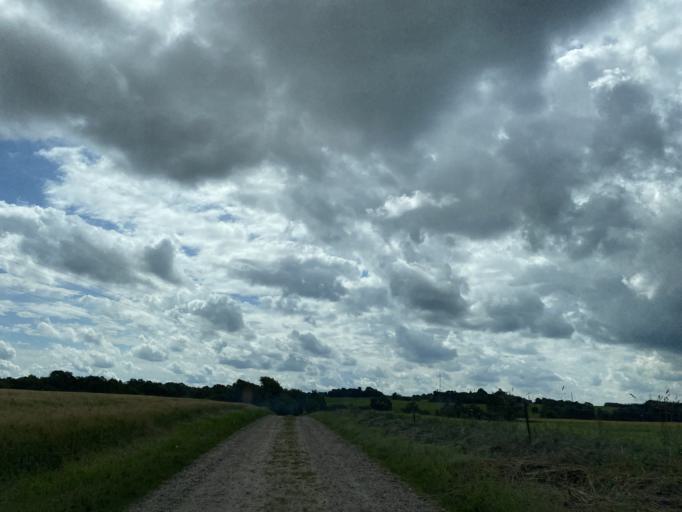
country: DK
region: Central Jutland
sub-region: Silkeborg Kommune
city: Silkeborg
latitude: 56.2189
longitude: 9.5687
